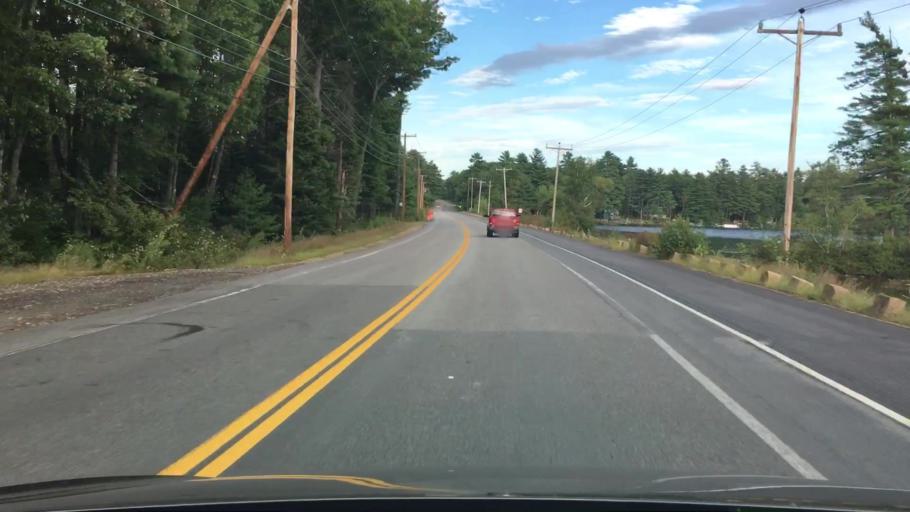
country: US
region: Maine
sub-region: Oxford County
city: Denmark
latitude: 44.0653
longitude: -70.8077
